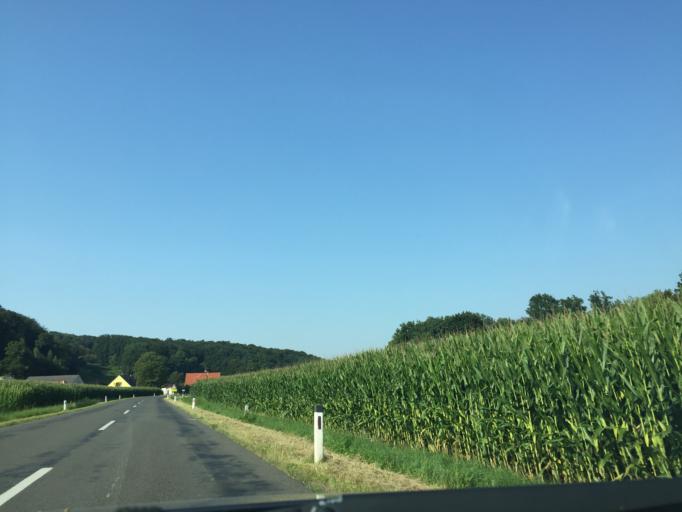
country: AT
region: Styria
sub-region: Politischer Bezirk Suedoststeiermark
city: Deutsch Goritz
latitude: 46.7577
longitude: 15.8397
